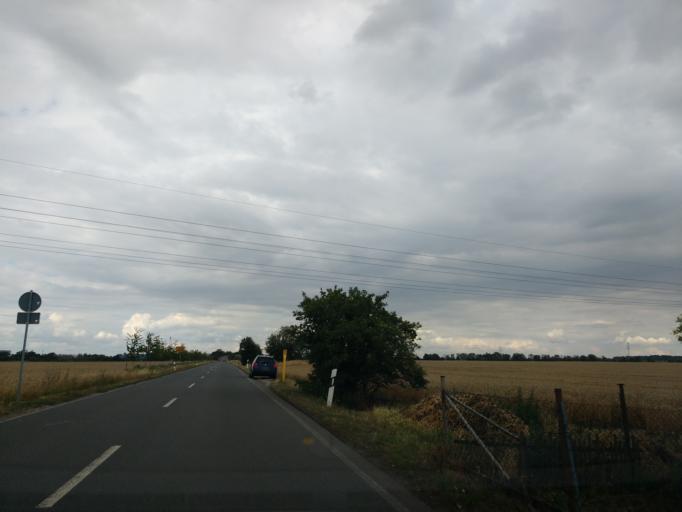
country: DE
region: Saxony-Anhalt
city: Dolbau
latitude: 51.4628
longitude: 12.0807
